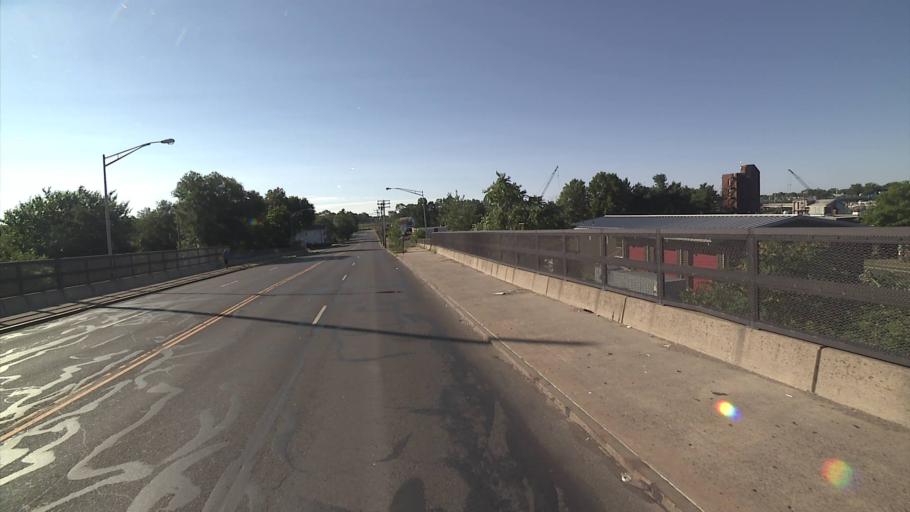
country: US
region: Connecticut
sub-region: New Haven County
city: West Haven
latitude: 41.2881
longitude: -72.9383
